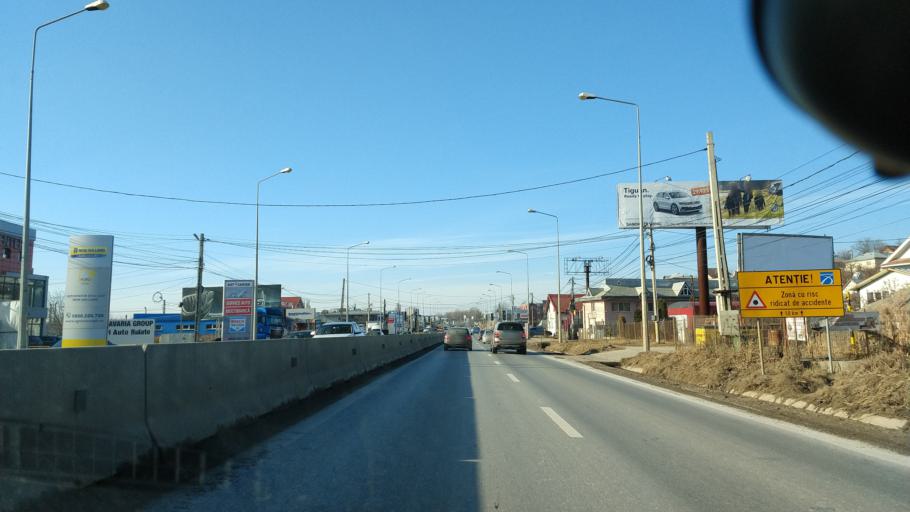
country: RO
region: Iasi
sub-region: Comuna Valea Lupului
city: Valea Lupului
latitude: 47.1743
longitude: 27.5041
